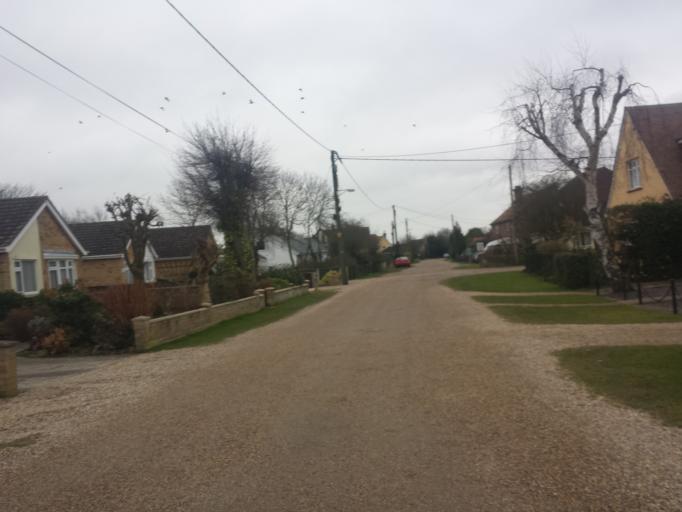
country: GB
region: England
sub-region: Essex
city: Little Clacton
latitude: 51.8608
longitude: 1.1604
